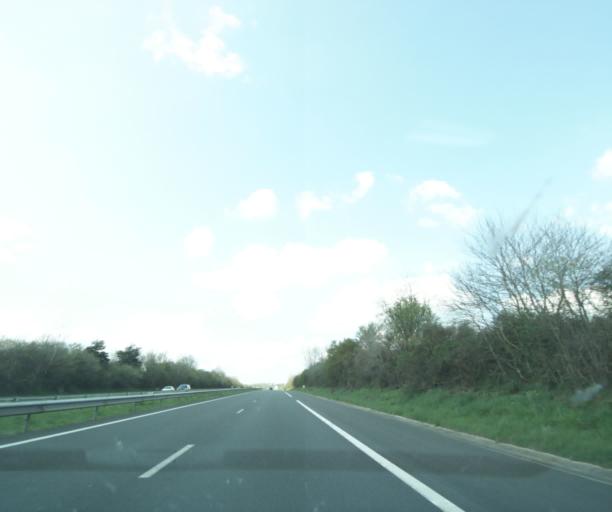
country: FR
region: Auvergne
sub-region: Departement de l'Allier
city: Bellenaves
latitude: 46.2761
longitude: 3.0537
